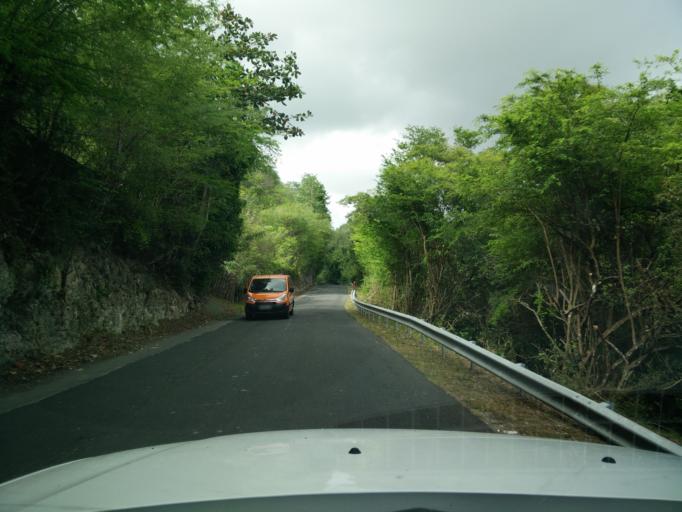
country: GP
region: Guadeloupe
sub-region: Guadeloupe
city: Le Gosier
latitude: 16.2202
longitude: -61.4754
